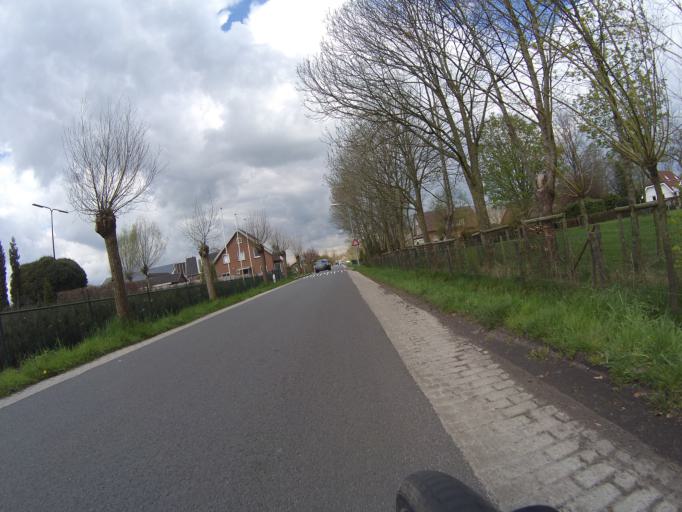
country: NL
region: Gelderland
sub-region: Gemeente Nijkerk
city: Nijkerk
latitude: 52.1927
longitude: 5.4543
